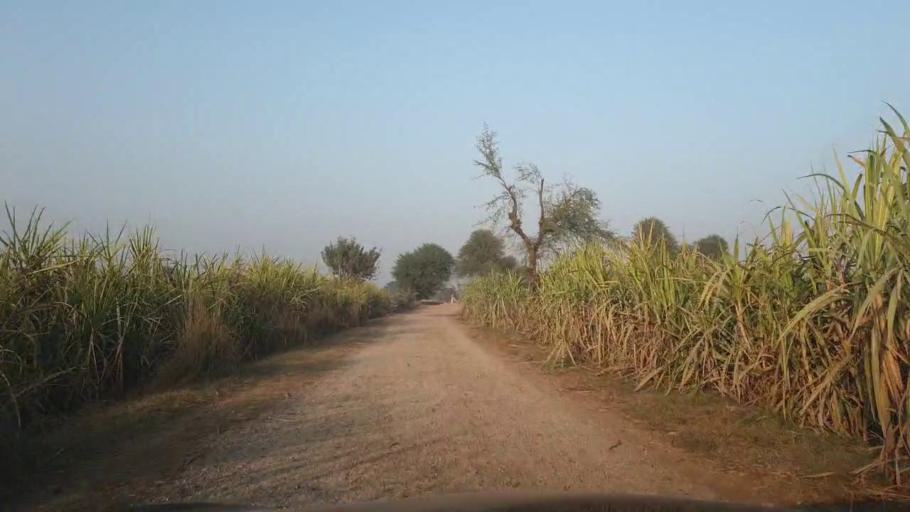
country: PK
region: Sindh
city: Ubauro
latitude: 28.3267
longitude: 69.7768
